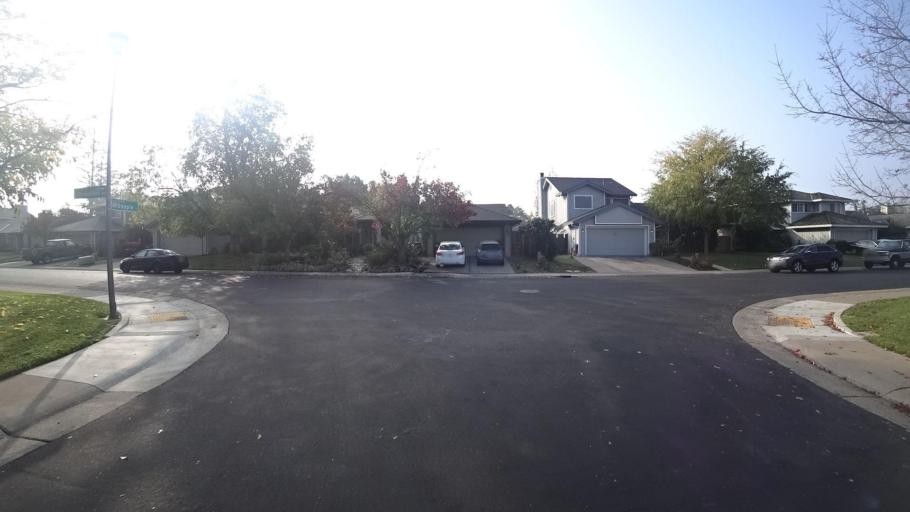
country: US
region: California
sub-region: Sacramento County
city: Elk Grove
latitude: 38.4103
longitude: -121.3549
